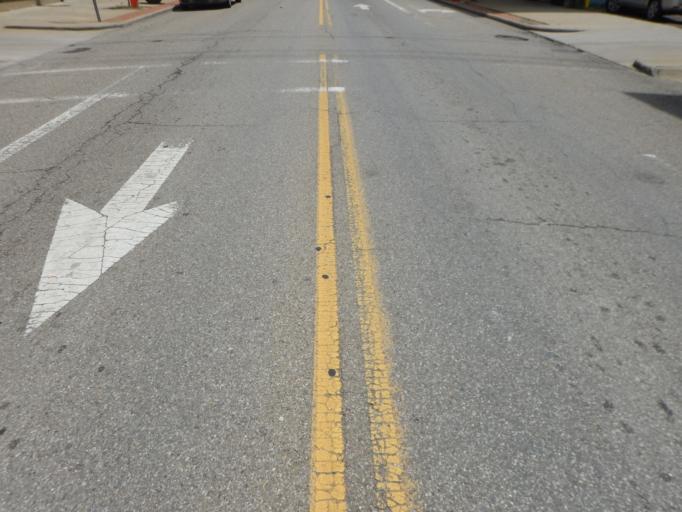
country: US
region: Ohio
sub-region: Muskingum County
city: Zanesville
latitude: 39.9401
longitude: -82.0048
